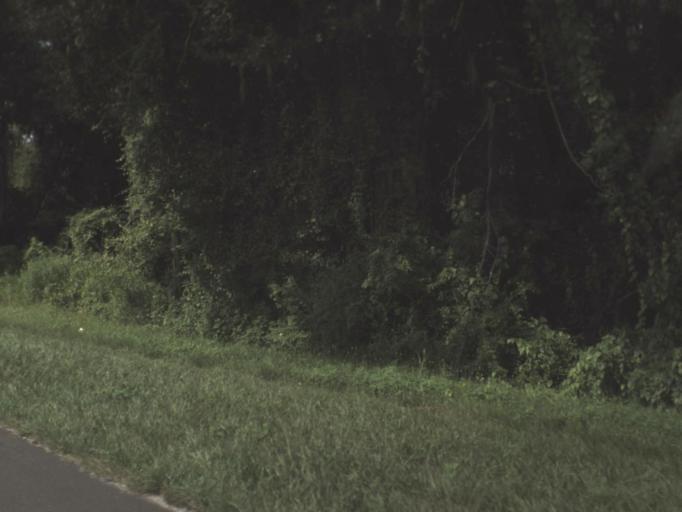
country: US
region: Florida
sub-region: Pasco County
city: Crystal Springs
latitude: 28.1738
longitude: -82.1565
